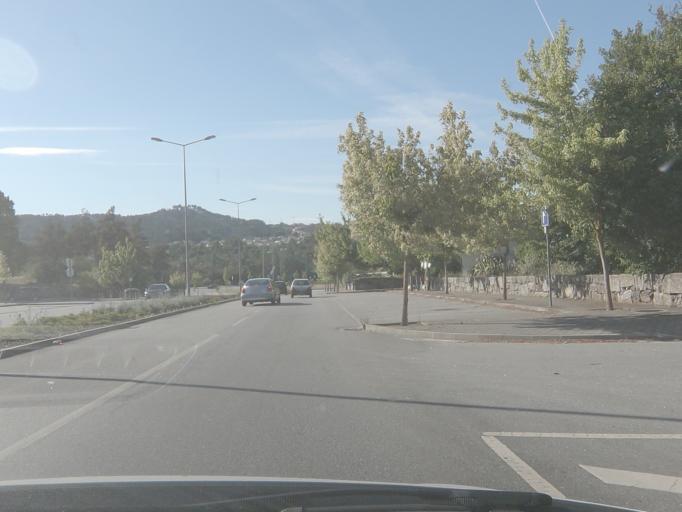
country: PT
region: Viseu
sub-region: Viseu
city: Abraveses
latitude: 40.6783
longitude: -7.9260
